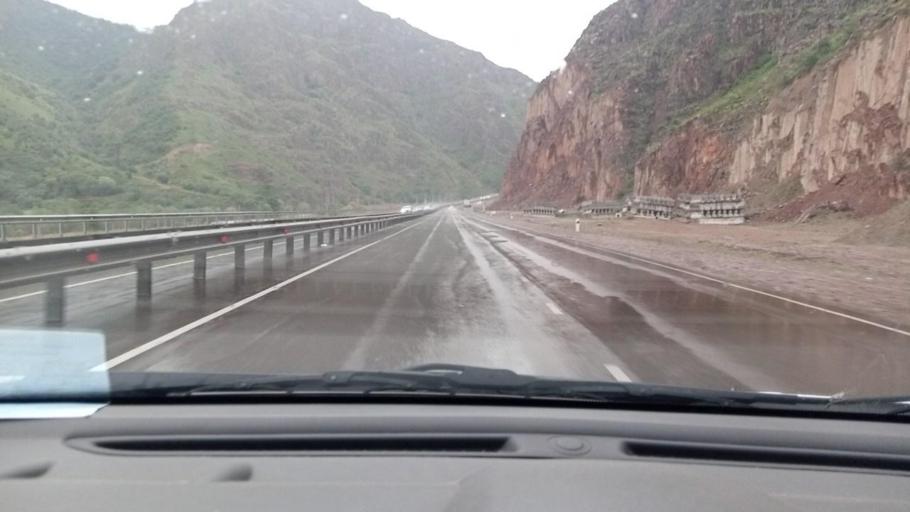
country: UZ
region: Toshkent
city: Angren
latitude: 41.0894
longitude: 70.3208
